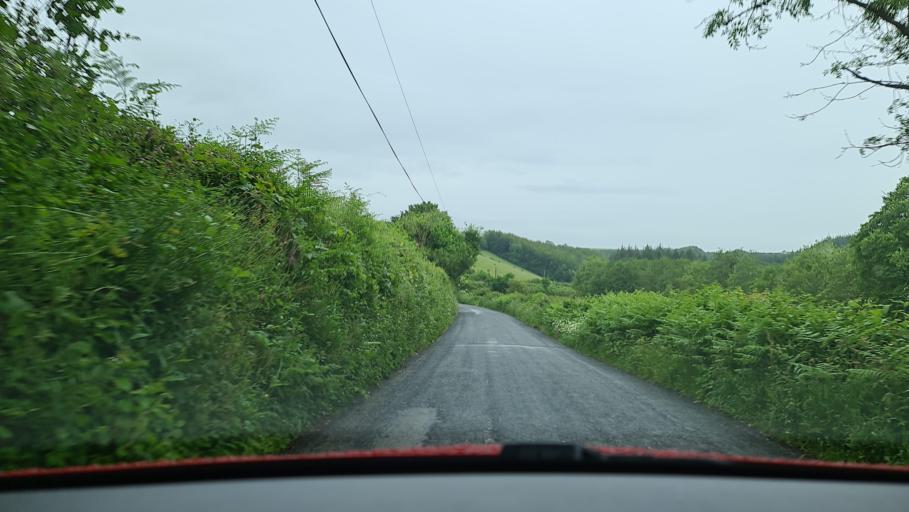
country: GB
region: England
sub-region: Cornwall
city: Liskeard
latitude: 50.4647
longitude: -4.5585
